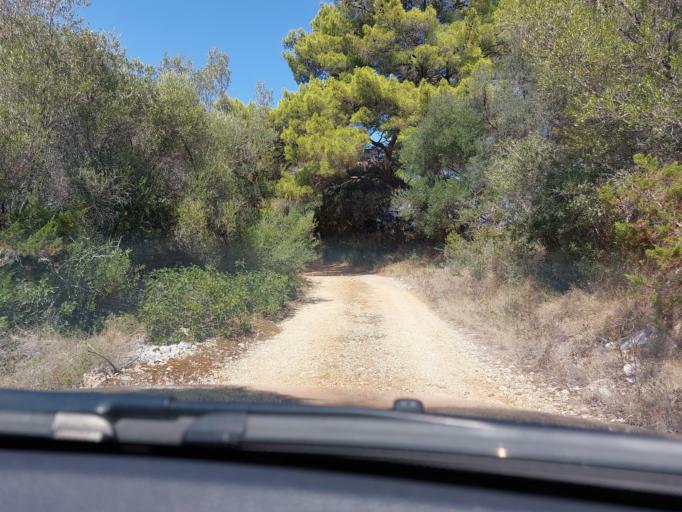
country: HR
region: Dubrovacko-Neretvanska
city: Smokvica
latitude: 42.7752
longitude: 16.8370
